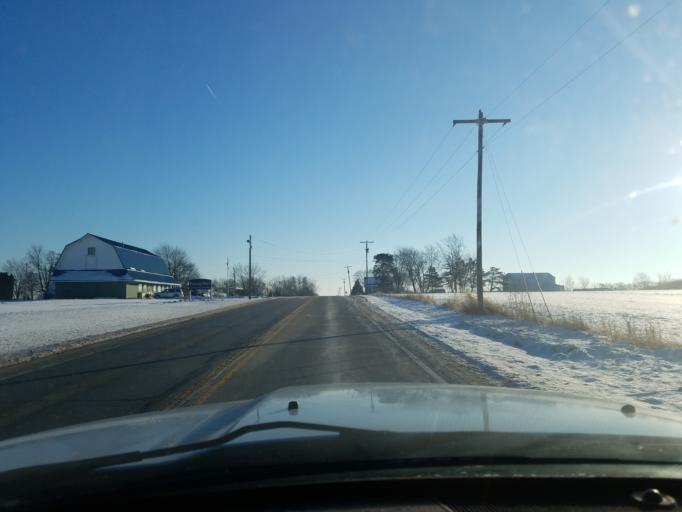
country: US
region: Indiana
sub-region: Noble County
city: Ligonier
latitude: 41.4523
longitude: -85.5751
